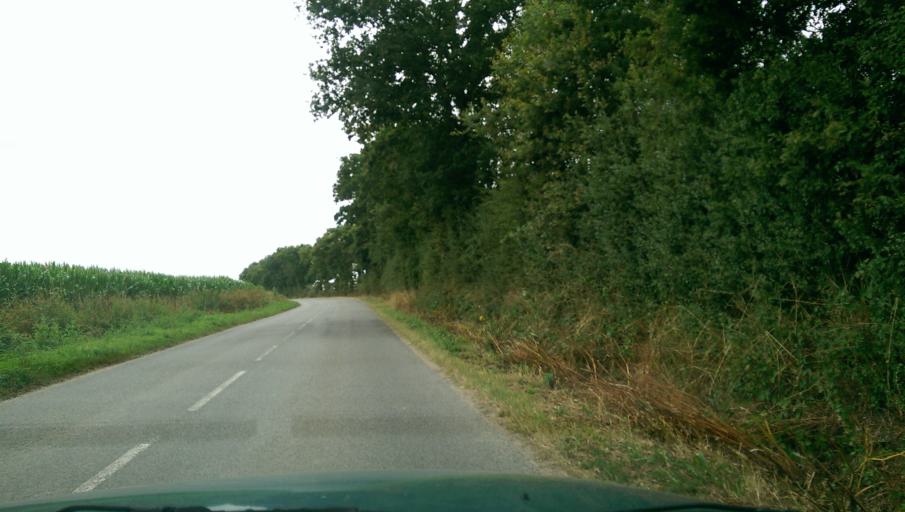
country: FR
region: Pays de la Loire
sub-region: Departement de la Loire-Atlantique
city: La Planche
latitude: 47.0076
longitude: -1.4280
